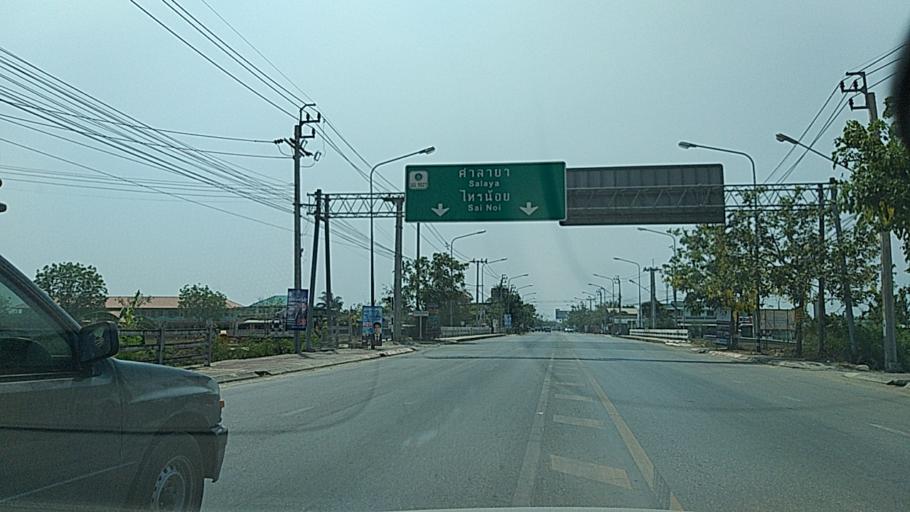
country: TH
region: Nonthaburi
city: Bang Yai
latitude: 13.9100
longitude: 100.3378
